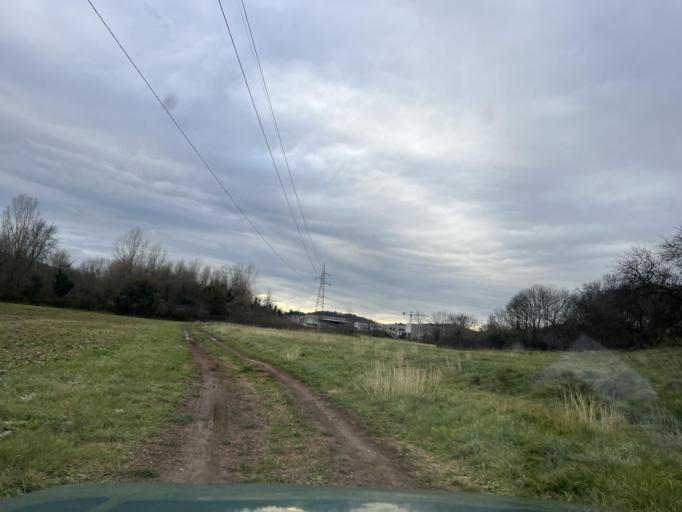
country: IT
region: Friuli Venezia Giulia
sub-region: Provincia di Gorizia
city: Savogna d'Isonzo
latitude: 45.9151
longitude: 13.5639
